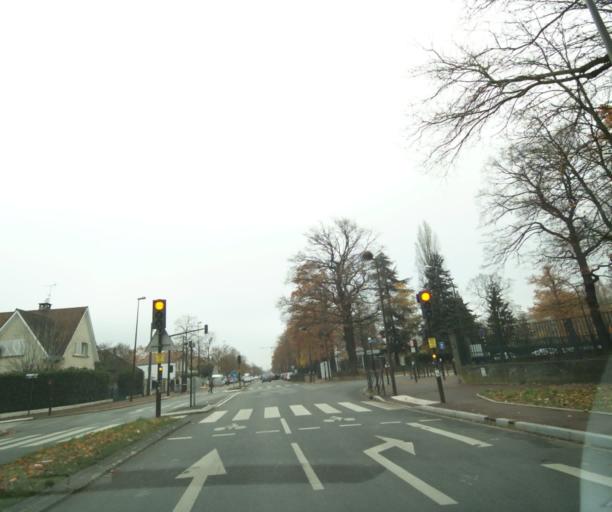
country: FR
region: Ile-de-France
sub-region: Departement de Seine-Saint-Denis
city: Livry-Gargan
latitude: 48.9186
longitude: 2.5283
